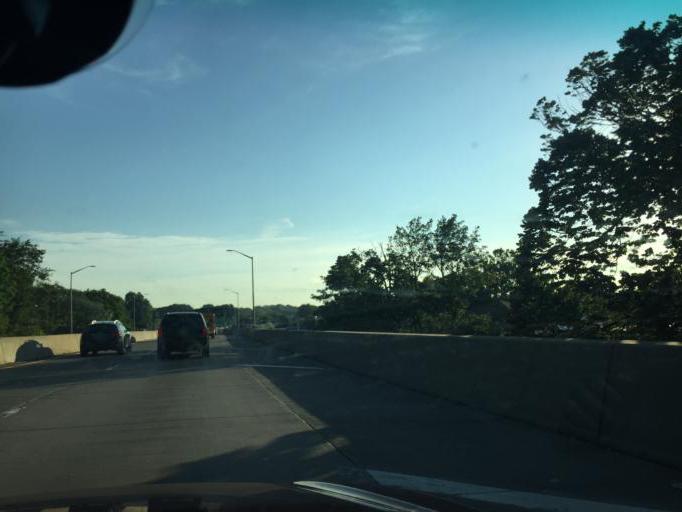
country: US
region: New York
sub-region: Queens County
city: Long Island City
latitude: 40.7590
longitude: -73.8992
